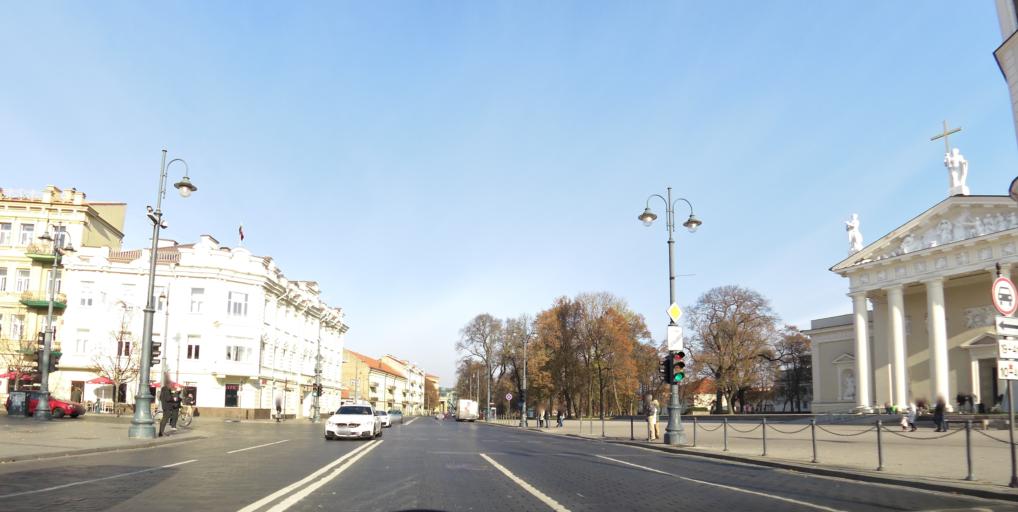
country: LT
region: Vilnius County
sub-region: Vilnius
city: Vilnius
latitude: 54.6856
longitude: 25.2860
